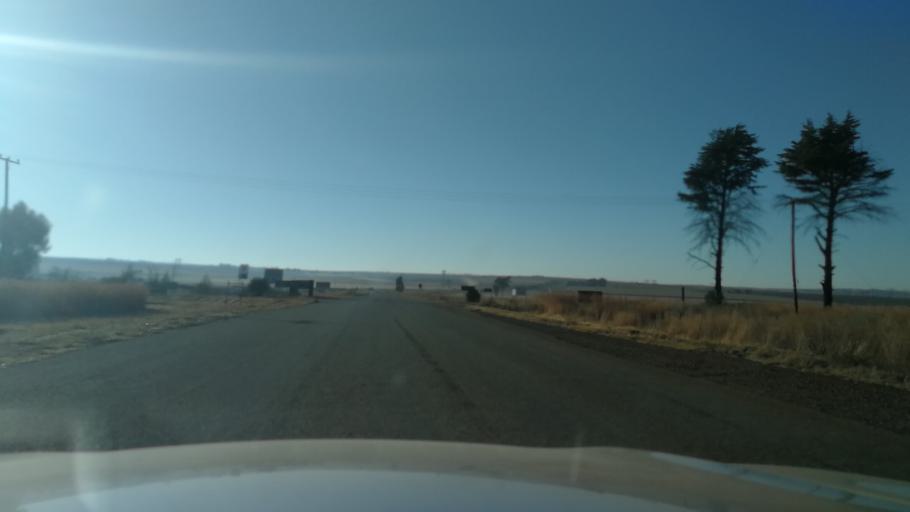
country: ZA
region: North-West
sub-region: Bojanala Platinum District Municipality
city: Rustenburg
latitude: -25.9717
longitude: 27.2350
